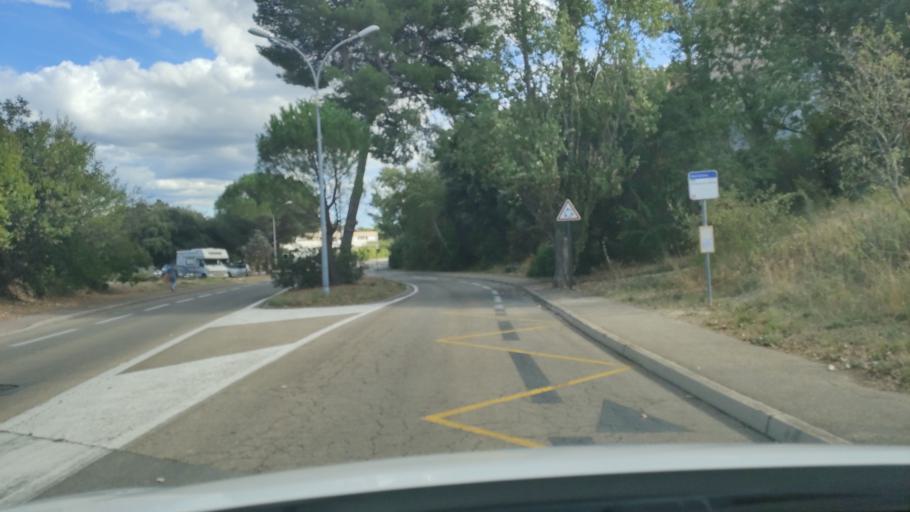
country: FR
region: Languedoc-Roussillon
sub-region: Departement du Gard
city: Les Angles
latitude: 43.9749
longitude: 4.7753
